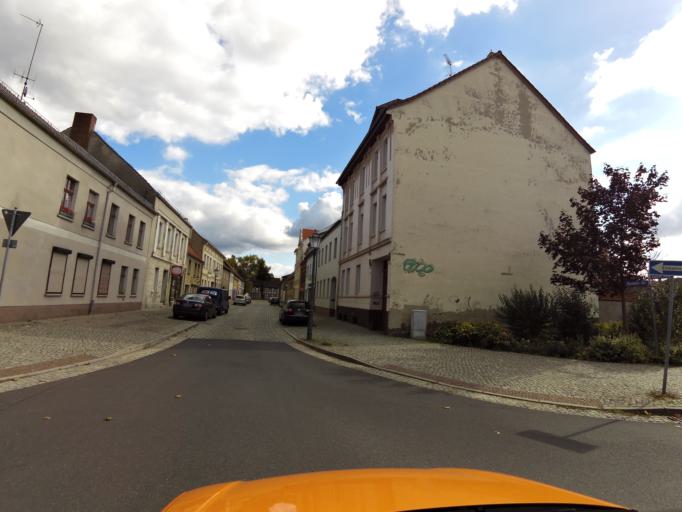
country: DE
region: Brandenburg
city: Luckenwalde
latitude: 52.0894
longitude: 13.1760
